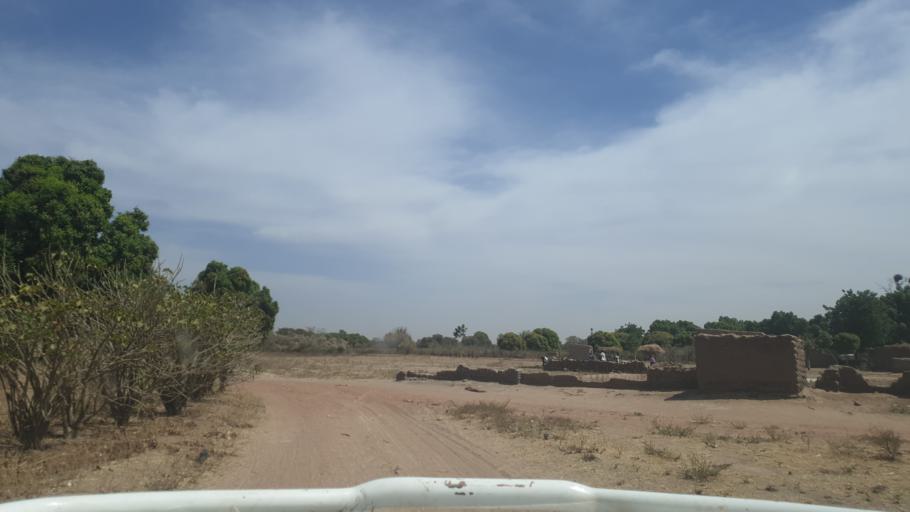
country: ML
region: Sikasso
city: Yorosso
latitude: 12.2822
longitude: -4.6847
